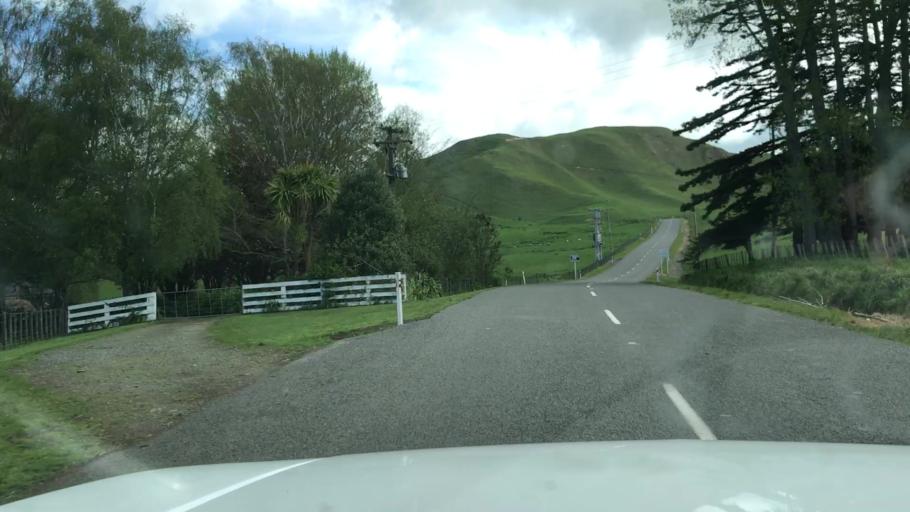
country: NZ
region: Hawke's Bay
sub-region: Hastings District
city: Hastings
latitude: -39.8208
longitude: 176.7375
